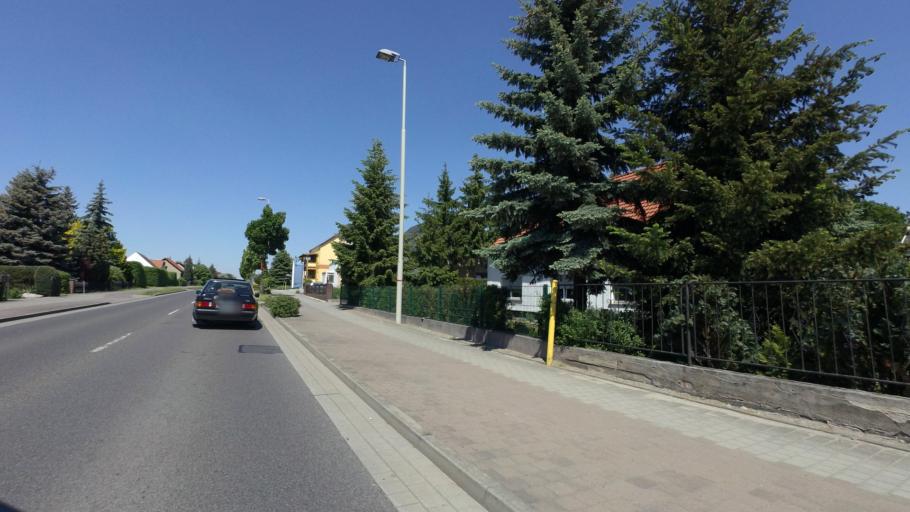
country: DE
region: Brandenburg
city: Cottbus
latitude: 51.7127
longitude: 14.3539
